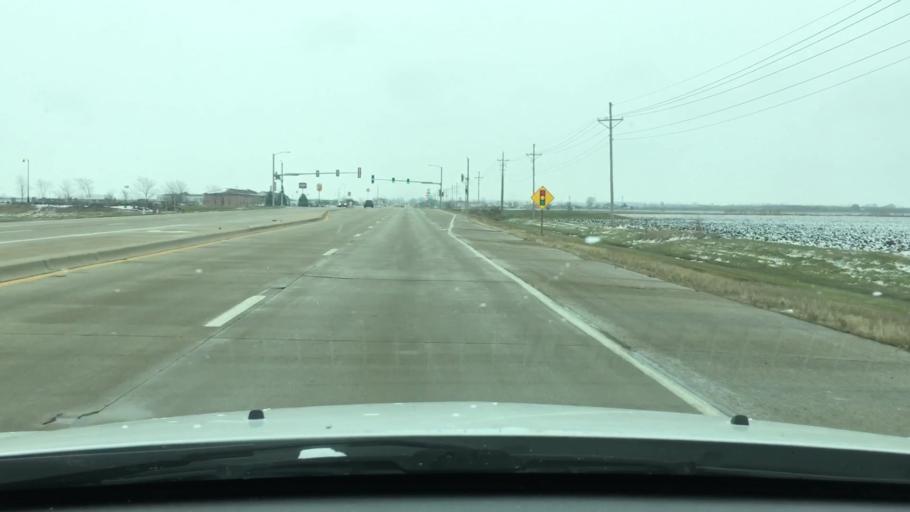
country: US
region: Illinois
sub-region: Ogle County
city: Rochelle
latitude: 41.9342
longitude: -89.0507
